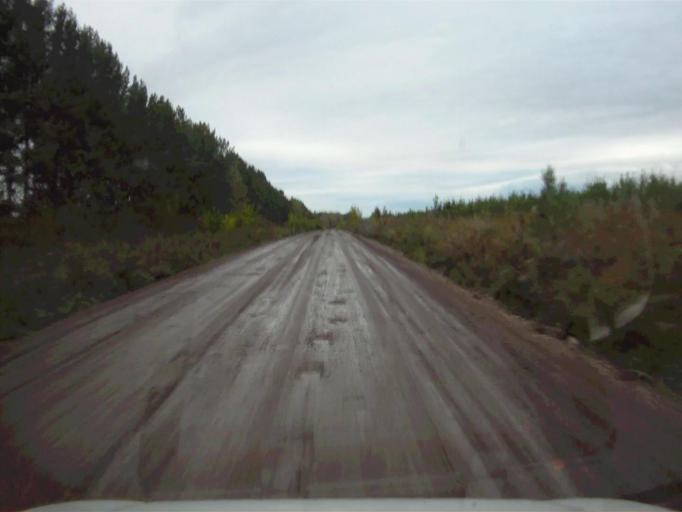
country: RU
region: Sverdlovsk
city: Mikhaylovsk
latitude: 56.1455
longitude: 59.2820
